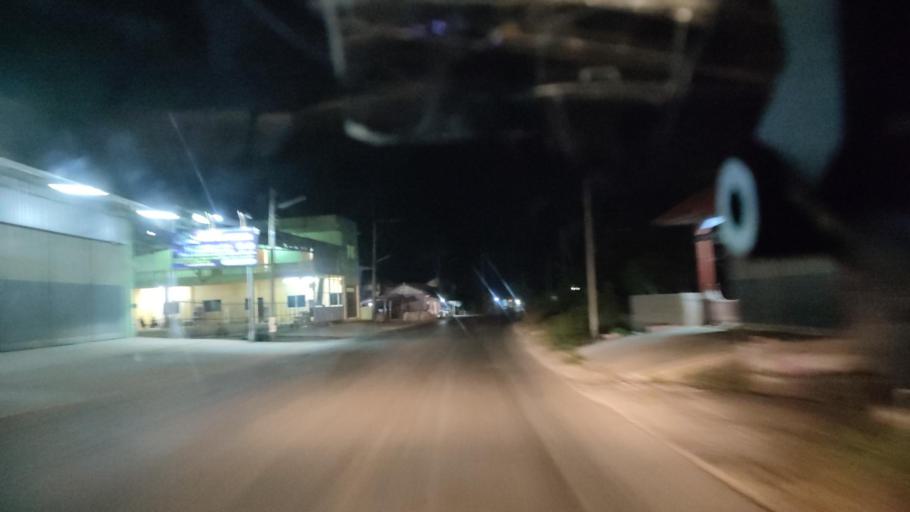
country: TH
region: Chiang Rai
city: Mae Sai
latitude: 20.5614
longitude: 99.9823
